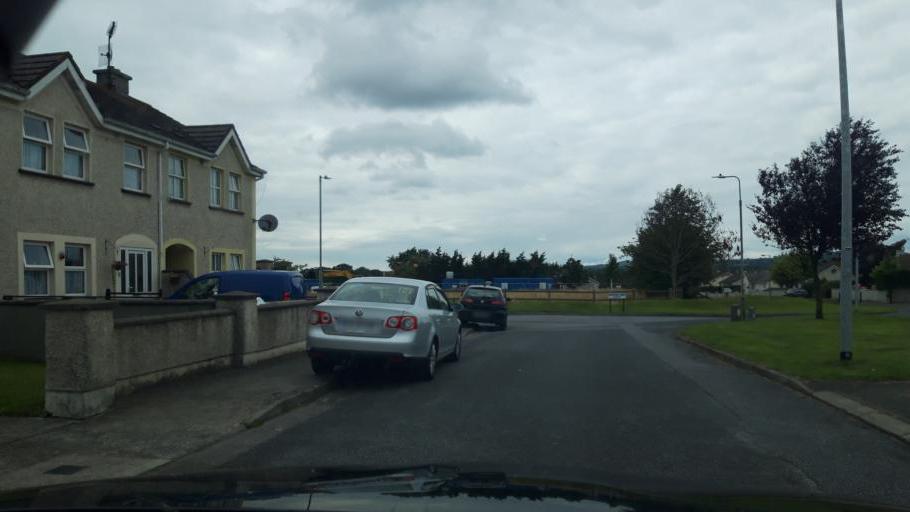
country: IE
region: Leinster
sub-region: County Carlow
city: Bagenalstown
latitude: 52.6309
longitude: -7.0652
